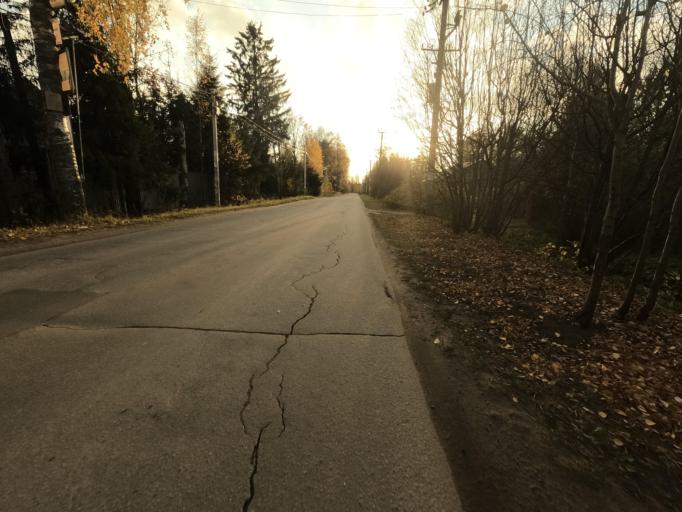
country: RU
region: St.-Petersburg
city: Beloostrov
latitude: 60.1734
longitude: 30.0175
